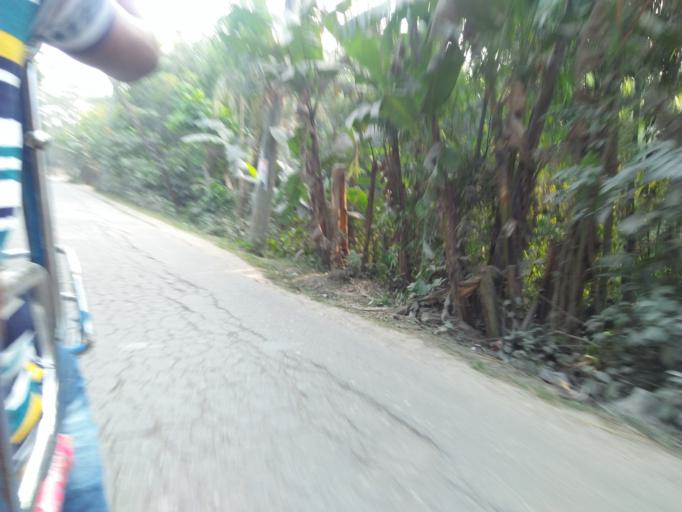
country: BD
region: Barisal
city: Bhola
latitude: 22.6974
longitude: 90.6433
